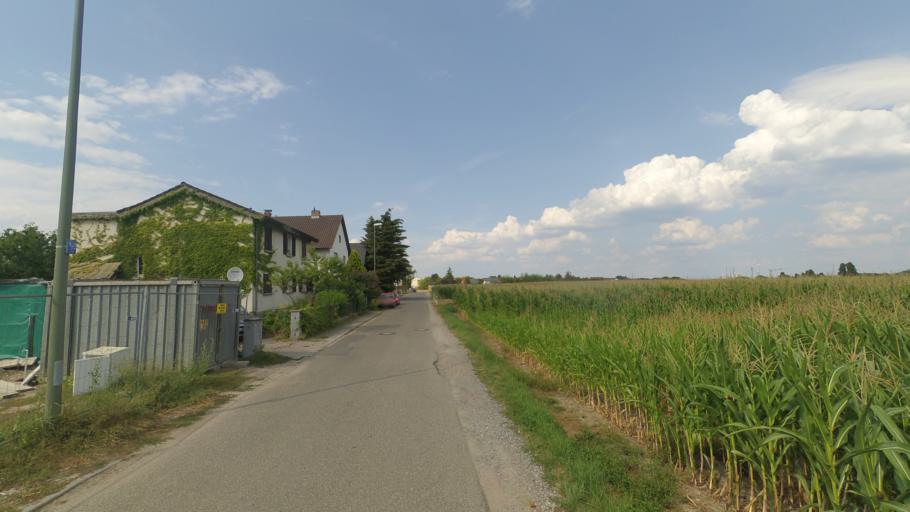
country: DE
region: Rheinland-Pfalz
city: Frankenthal
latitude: 49.5198
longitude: 8.3831
